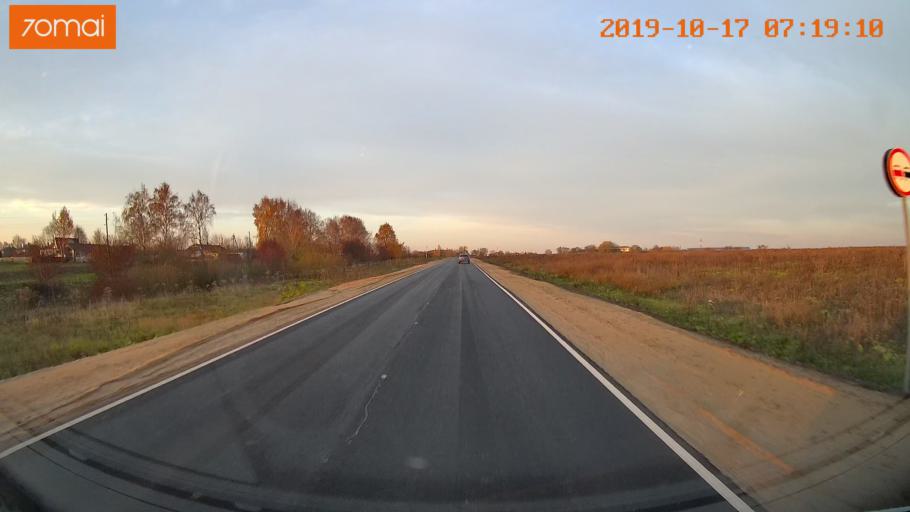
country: RU
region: Ivanovo
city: Gavrilov Posad
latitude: 56.3470
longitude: 40.2048
